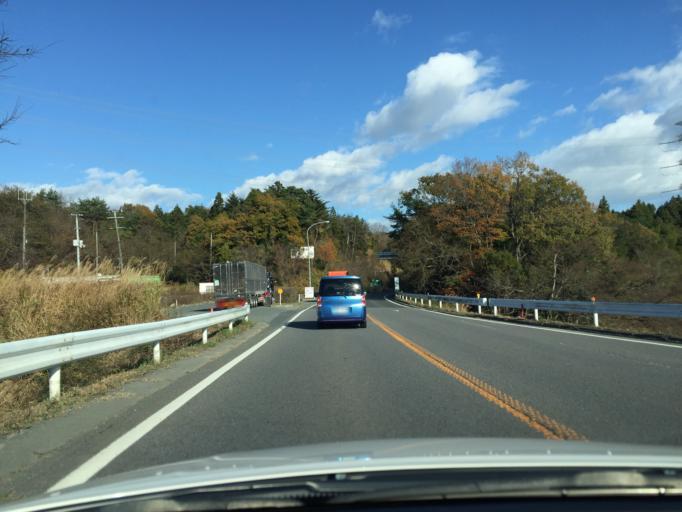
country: JP
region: Fukushima
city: Namie
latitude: 37.3138
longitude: 141.0007
